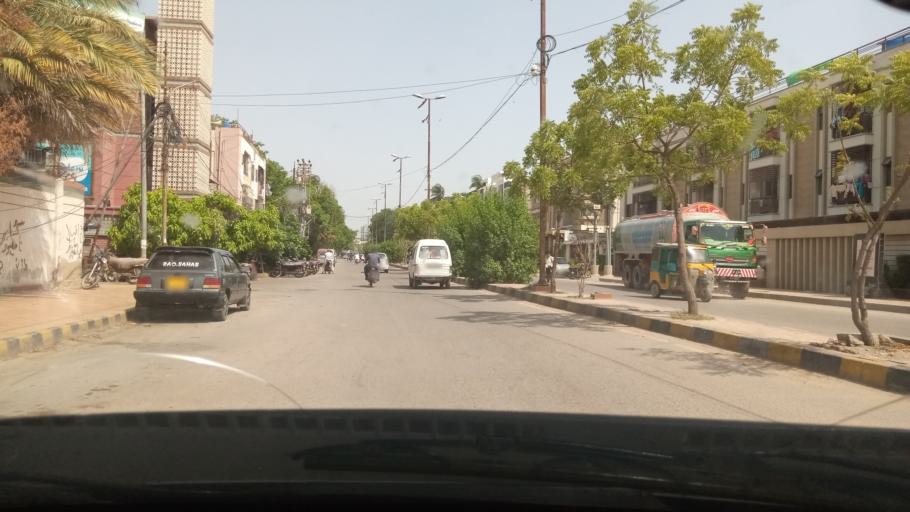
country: PK
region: Sindh
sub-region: Karachi District
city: Karachi
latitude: 24.8768
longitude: 67.0442
